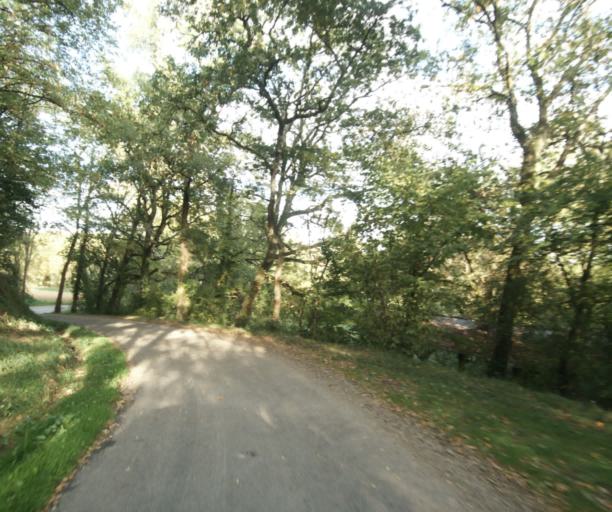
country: FR
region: Midi-Pyrenees
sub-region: Departement du Gers
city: Gondrin
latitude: 43.8899
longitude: 0.2940
